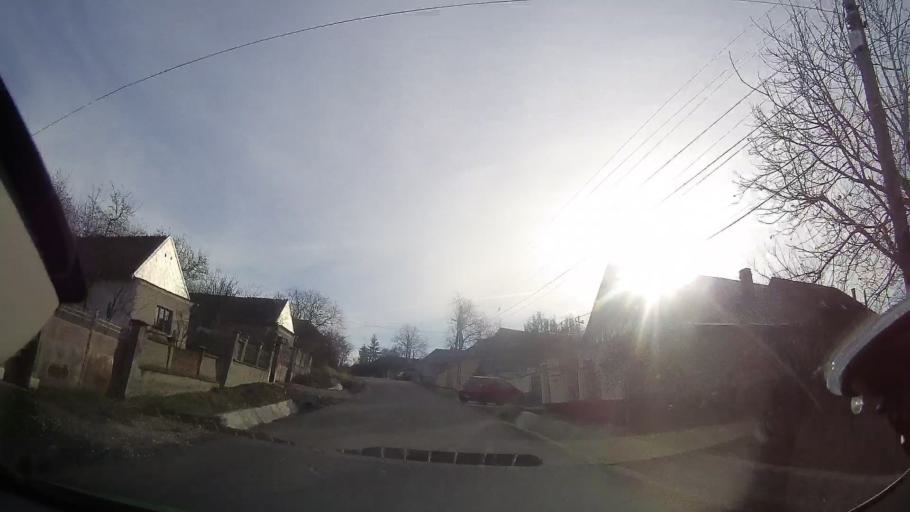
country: RO
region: Bihor
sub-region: Comuna Sarbi
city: Burzuc
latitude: 47.1748
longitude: 22.1529
